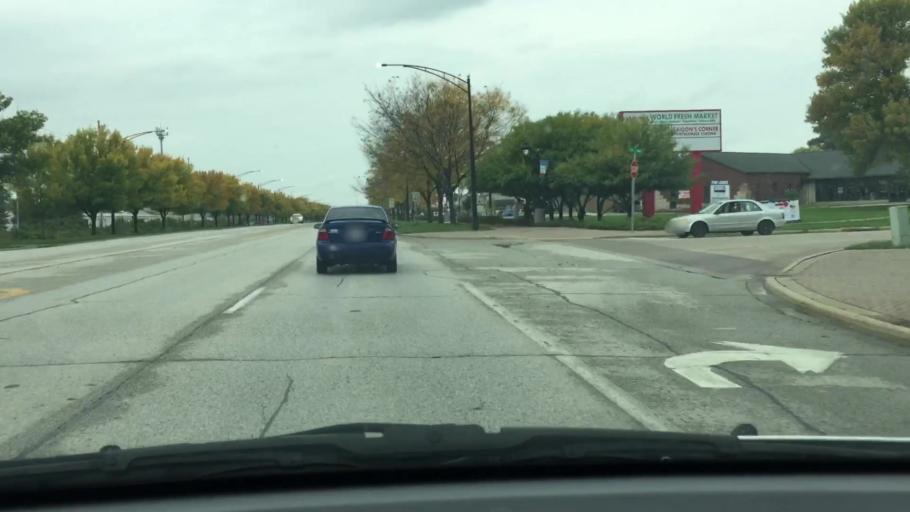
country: US
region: Iowa
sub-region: Johnson County
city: Coralville
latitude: 41.6828
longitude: -91.5977
